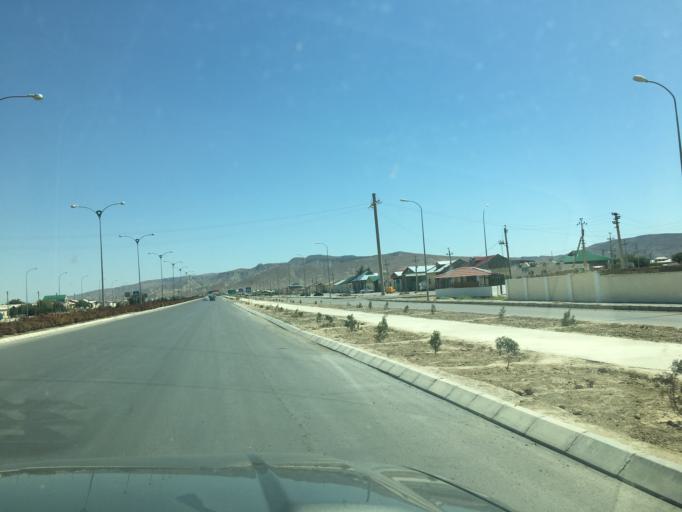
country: TM
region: Balkan
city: Serdar
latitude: 38.9887
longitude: 56.2887
